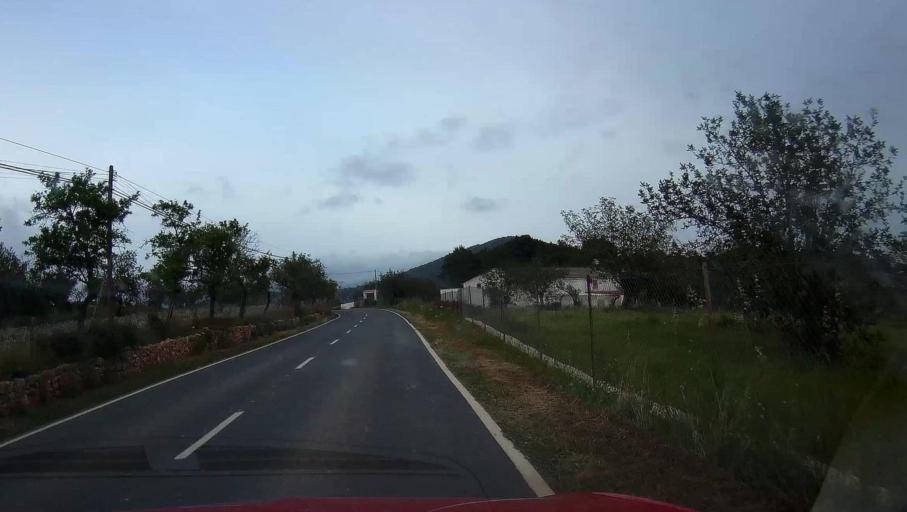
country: ES
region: Balearic Islands
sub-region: Illes Balears
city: Sant Joan de Labritja
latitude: 39.0497
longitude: 1.4313
